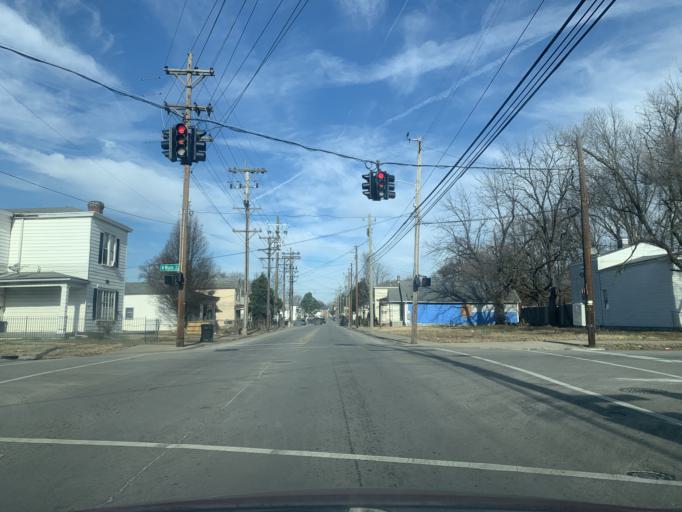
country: US
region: Kentucky
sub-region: Jefferson County
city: Louisville
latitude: 38.2606
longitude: -85.7936
